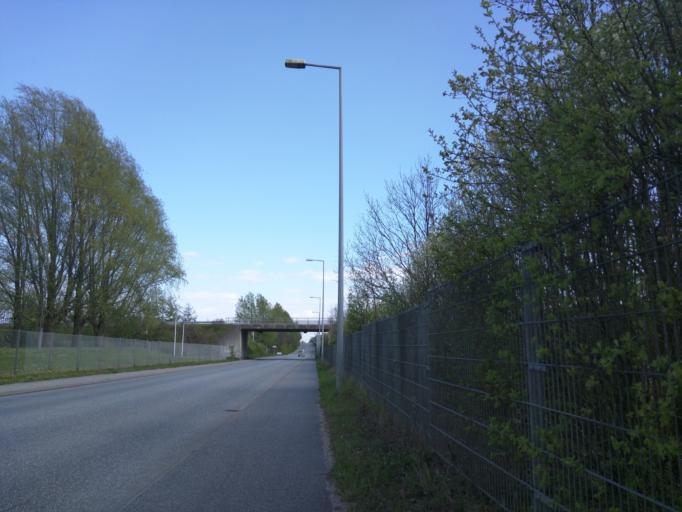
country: DK
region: South Denmark
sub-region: Fredericia Kommune
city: Snoghoj
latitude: 55.5406
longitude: 9.6994
